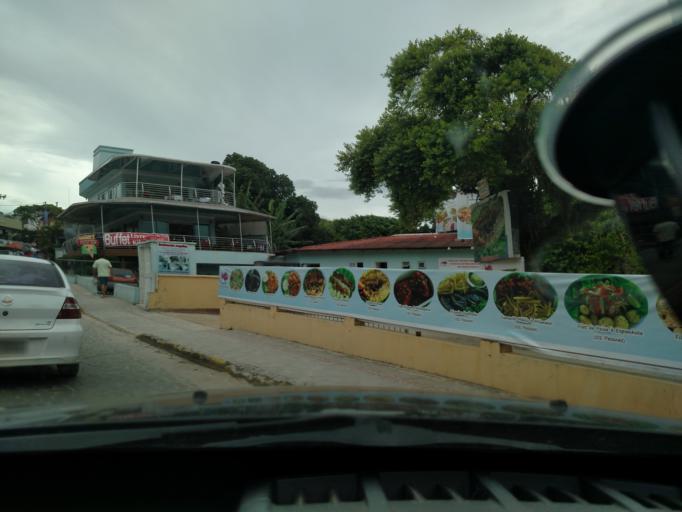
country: BR
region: Santa Catarina
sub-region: Porto Belo
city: Porto Belo
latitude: -27.1490
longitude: -48.4842
